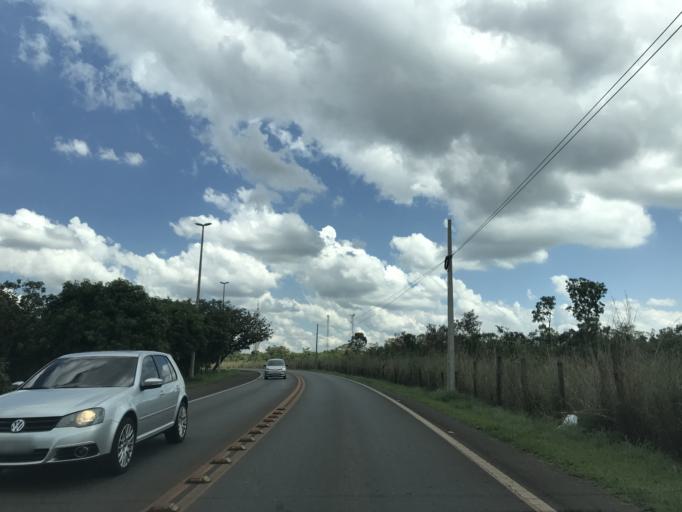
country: BR
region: Federal District
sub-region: Brasilia
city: Brasilia
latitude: -15.6864
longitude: -47.8375
